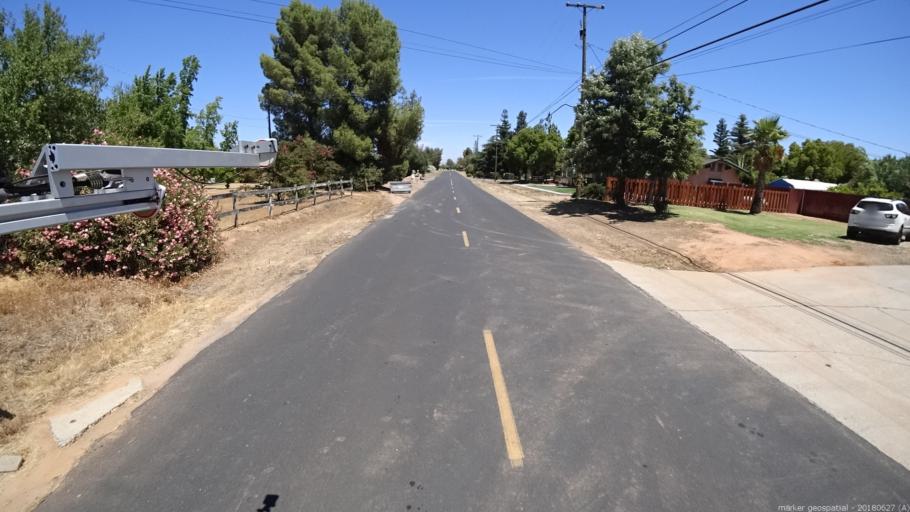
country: US
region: California
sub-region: Madera County
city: Bonadelle Ranchos-Madera Ranchos
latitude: 36.9285
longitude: -119.8700
